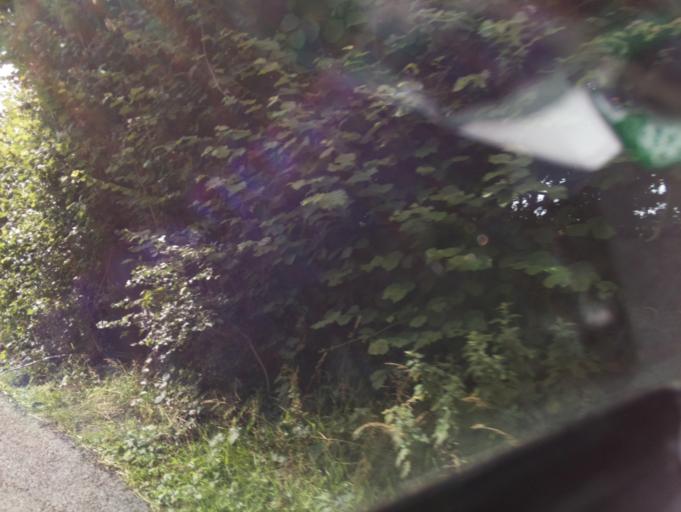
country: GB
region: England
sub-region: Gloucestershire
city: Newent
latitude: 51.8413
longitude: -2.3582
